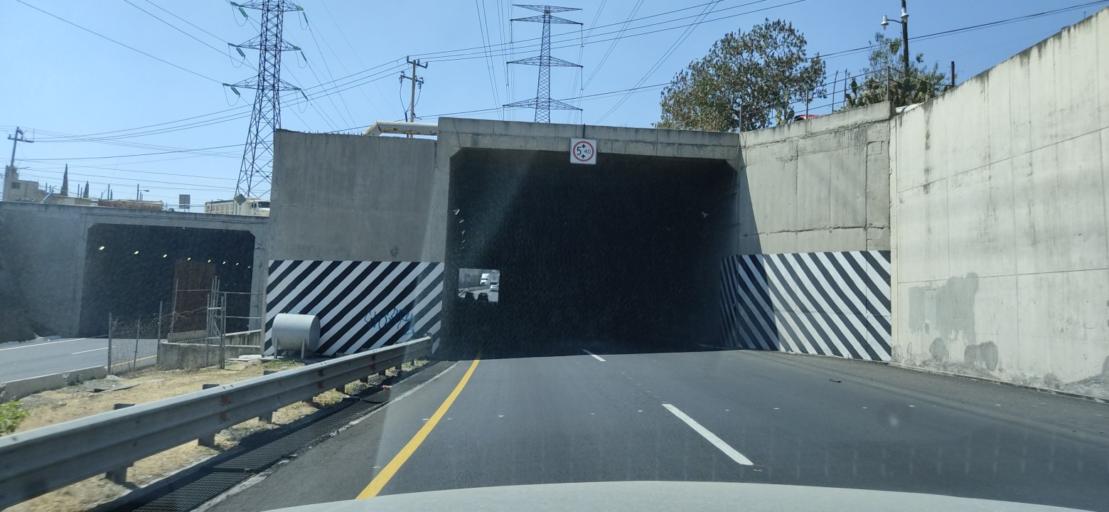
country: MX
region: Mexico
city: Cuautitlan Izcalli
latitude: 19.6227
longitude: -99.2219
